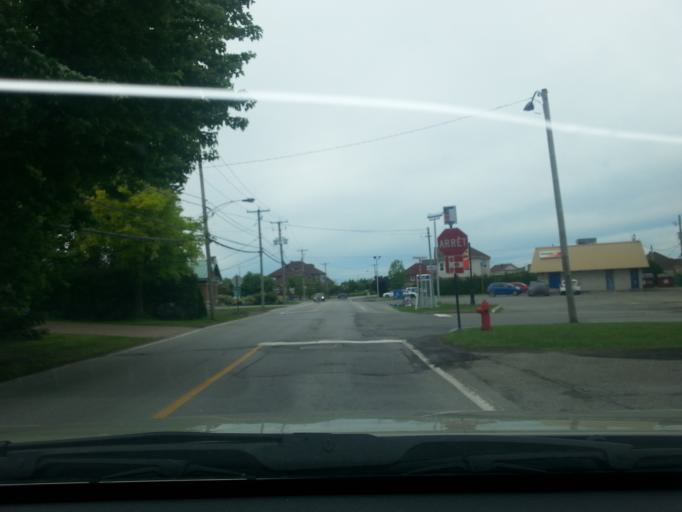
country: CA
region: Quebec
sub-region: Lanaudiere
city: Charlemagne
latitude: 45.7062
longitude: -73.5186
